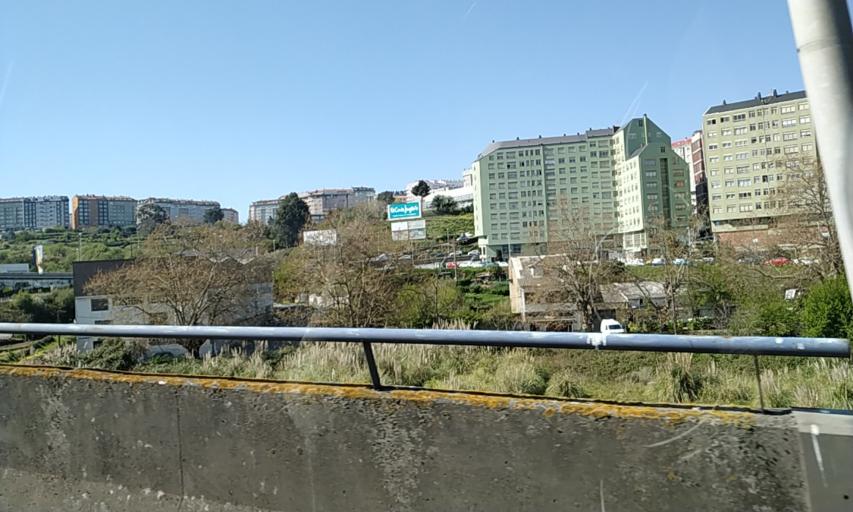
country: ES
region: Galicia
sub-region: Provincia da Coruna
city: A Coruna
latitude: 43.3490
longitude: -8.3886
